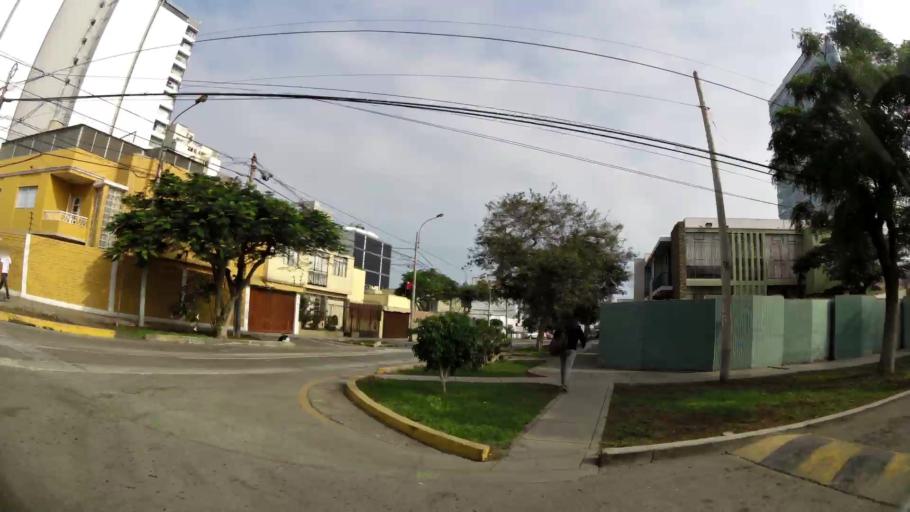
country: PE
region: Lima
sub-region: Lima
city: San Isidro
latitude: -12.0920
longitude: -77.0602
